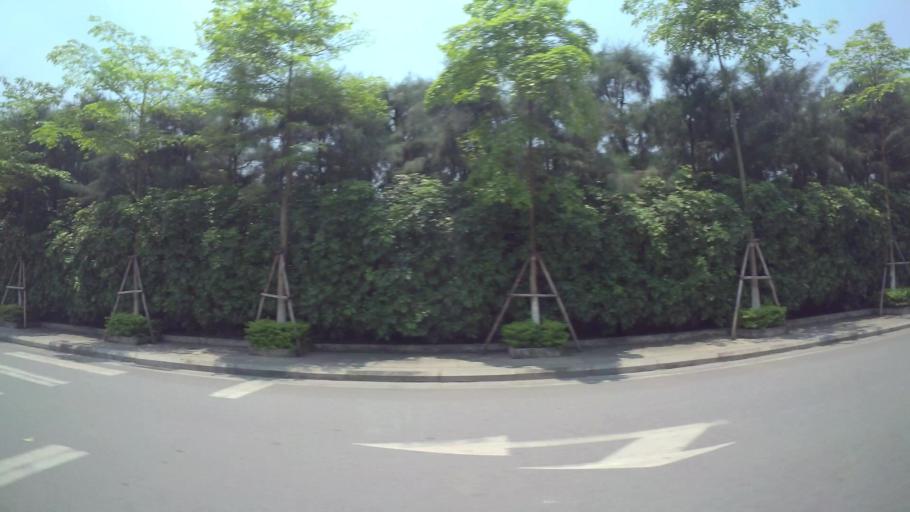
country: VN
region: Ha Noi
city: Trau Quy
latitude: 21.0358
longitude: 105.8963
